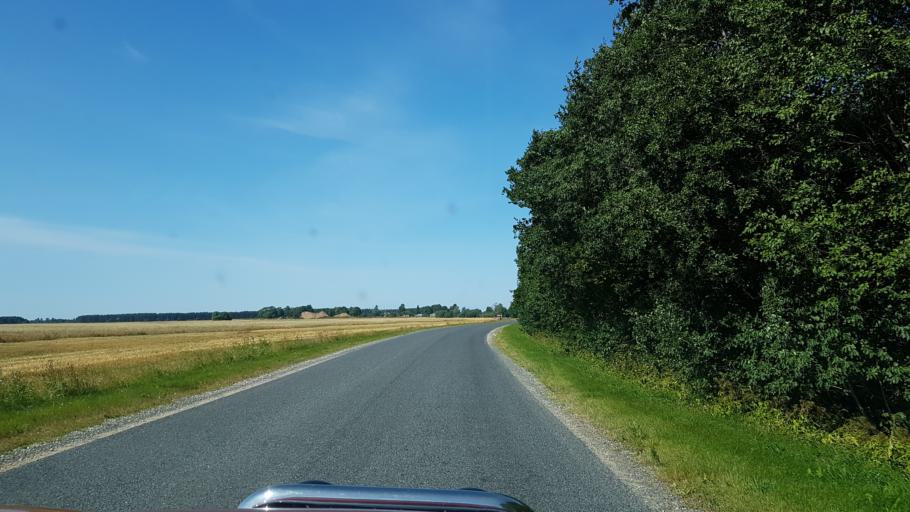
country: EE
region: Laeaene-Virumaa
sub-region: Rakke vald
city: Rakke
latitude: 59.0265
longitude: 26.3512
